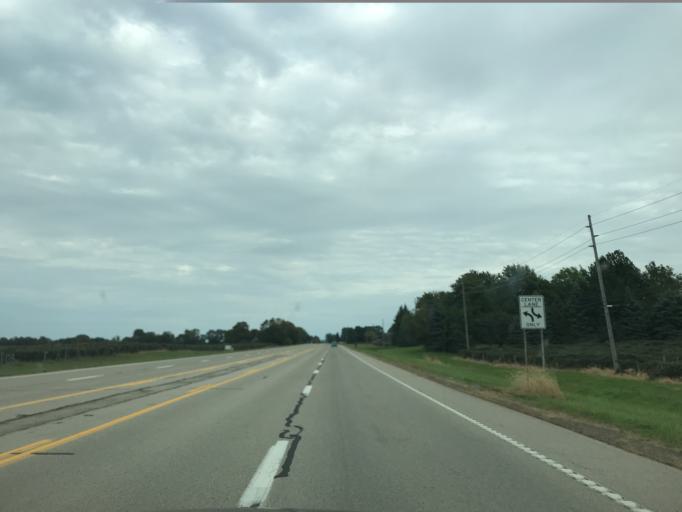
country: US
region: Pennsylvania
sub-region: Erie County
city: North East
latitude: 42.2228
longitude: -79.8120
